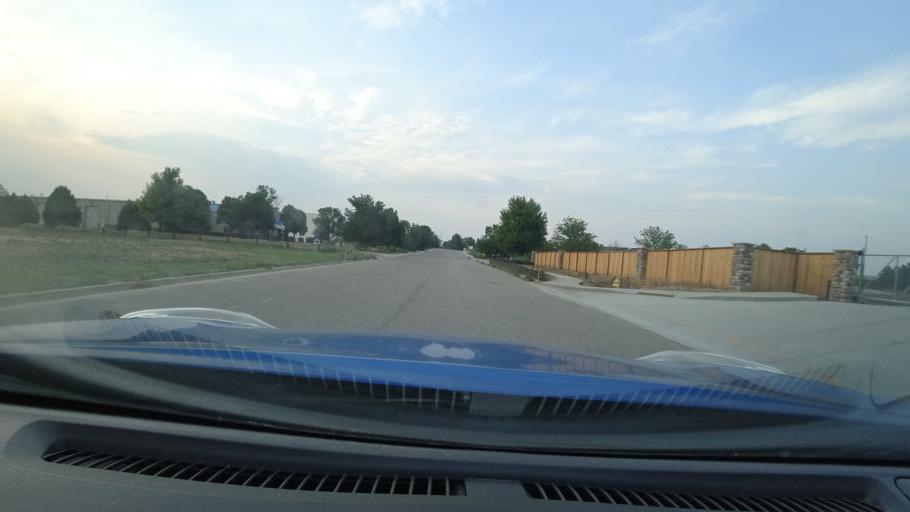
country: US
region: Colorado
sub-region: Adams County
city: Aurora
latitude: 39.7265
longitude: -104.7788
